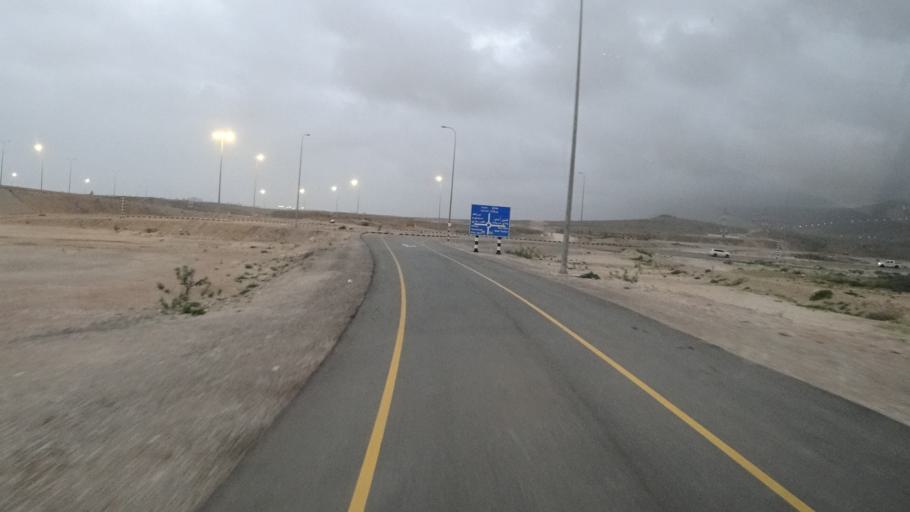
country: OM
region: Zufar
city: Salalah
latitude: 17.0607
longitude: 54.4327
